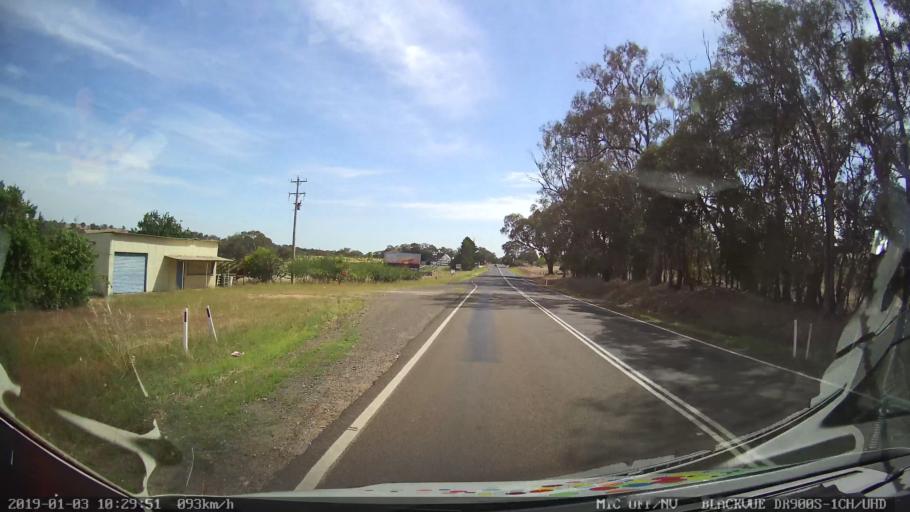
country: AU
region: New South Wales
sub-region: Young
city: Young
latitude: -34.3688
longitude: 148.2620
